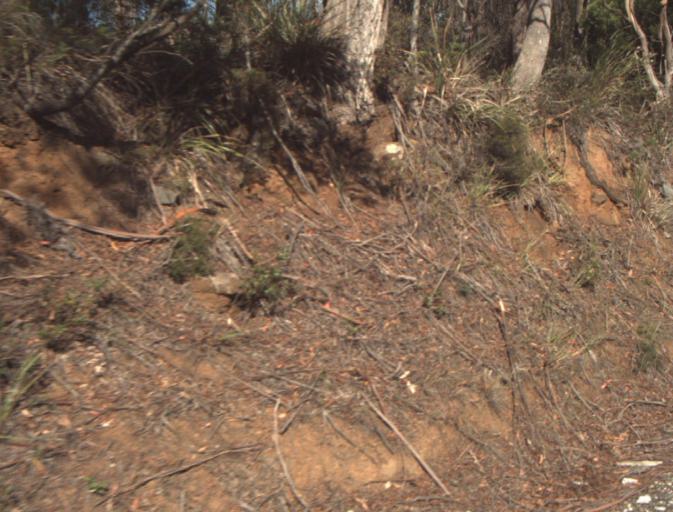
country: AU
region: Tasmania
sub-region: Launceston
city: Mayfield
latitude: -41.3010
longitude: 147.1334
